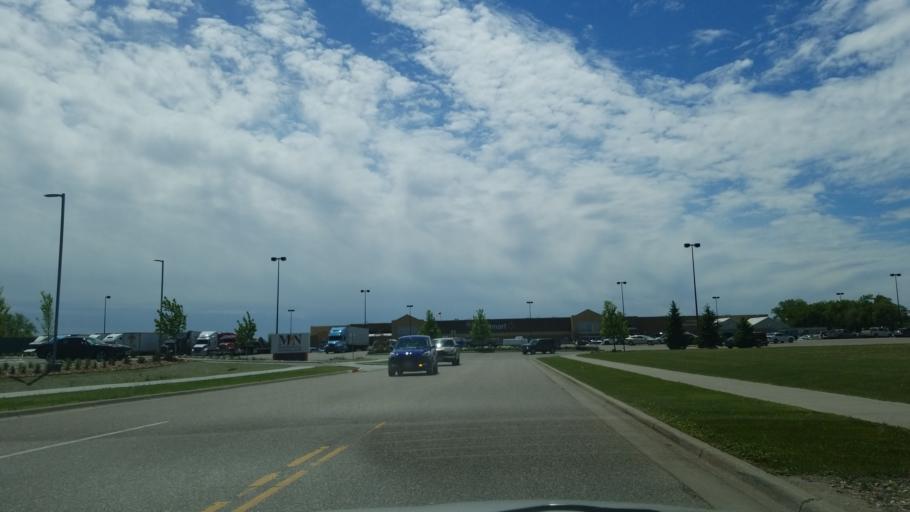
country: US
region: Minnesota
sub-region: Stearns County
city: Sauk Centre
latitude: 45.7228
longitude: -94.9471
